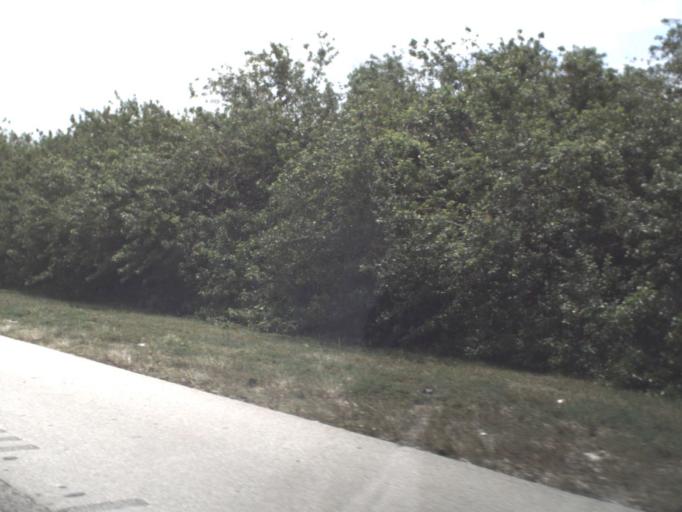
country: US
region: Florida
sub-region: Brevard County
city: Rockledge
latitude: 28.2758
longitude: -80.7318
